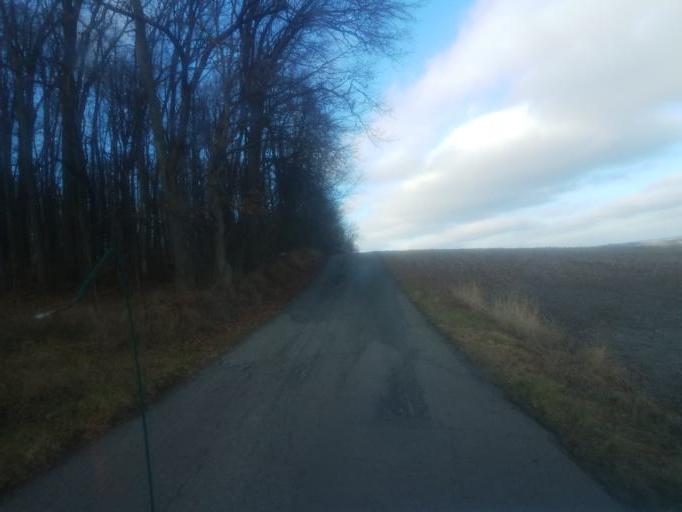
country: US
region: Ohio
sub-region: Ashland County
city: Loudonville
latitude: 40.6252
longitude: -82.3673
